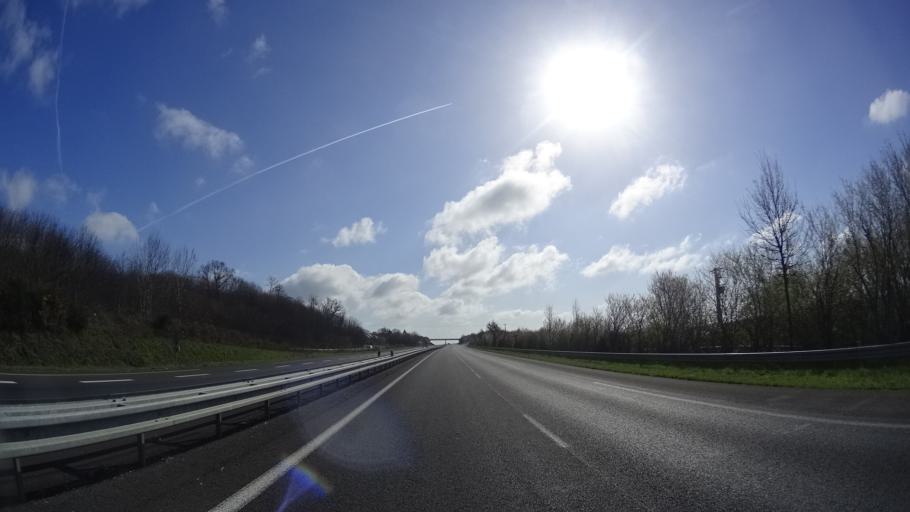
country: FR
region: Pays de la Loire
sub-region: Departement de Maine-et-Loire
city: Nyoiseau
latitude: 47.7002
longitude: -0.9330
